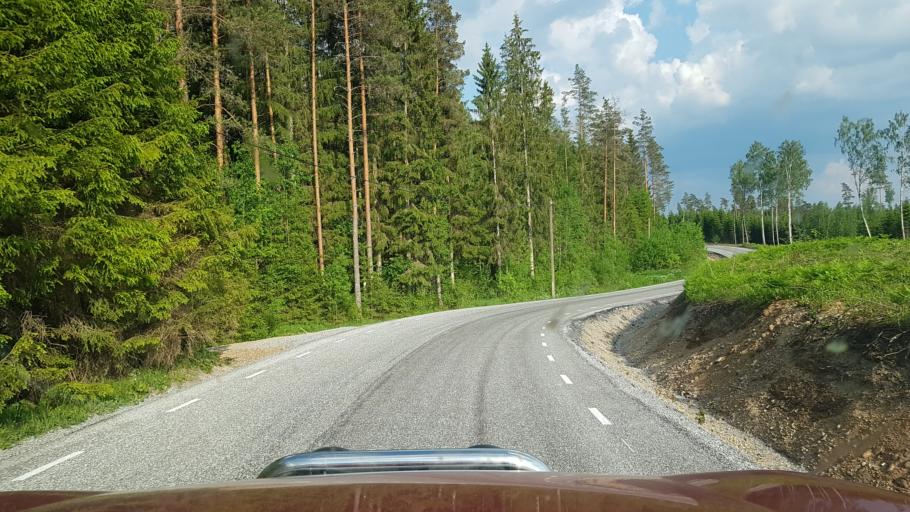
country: EE
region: Tartu
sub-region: UElenurme vald
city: Ulenurme
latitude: 58.1105
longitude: 26.7423
